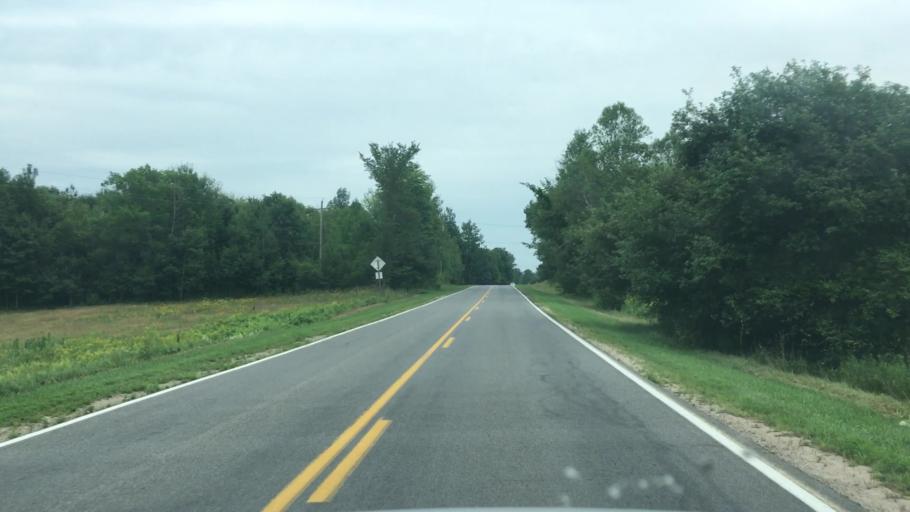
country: US
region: New York
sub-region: Clinton County
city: Morrisonville
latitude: 44.6112
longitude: -73.6380
